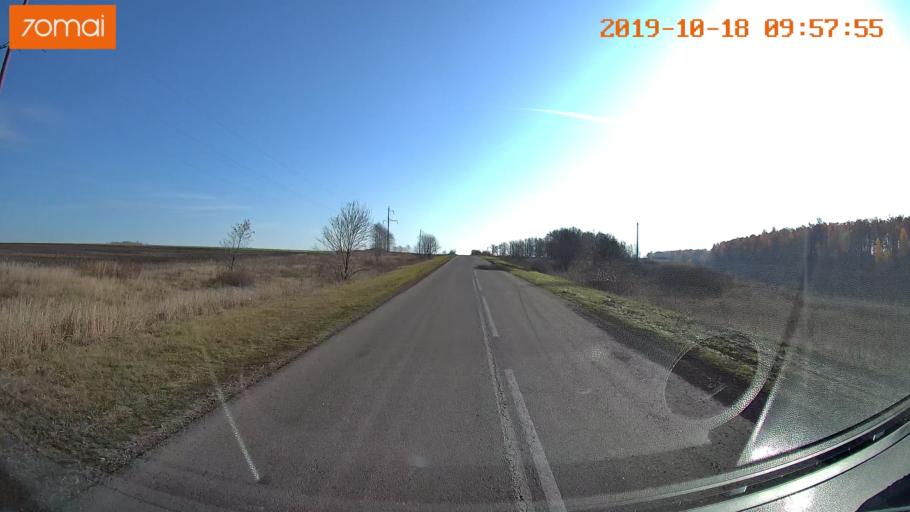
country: RU
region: Tula
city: Kurkino
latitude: 53.3765
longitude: 38.4286
